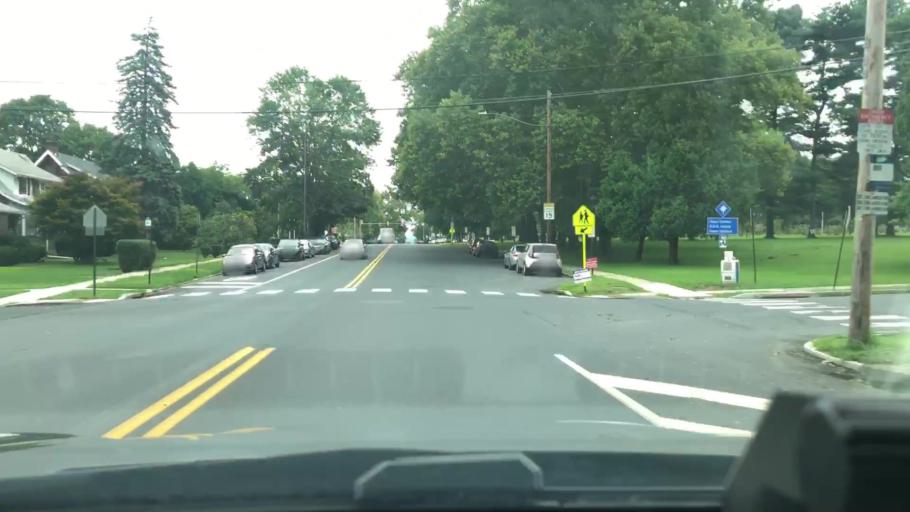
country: US
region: Pennsylvania
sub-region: Lehigh County
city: Fountain Hill
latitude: 40.6254
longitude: -75.3978
